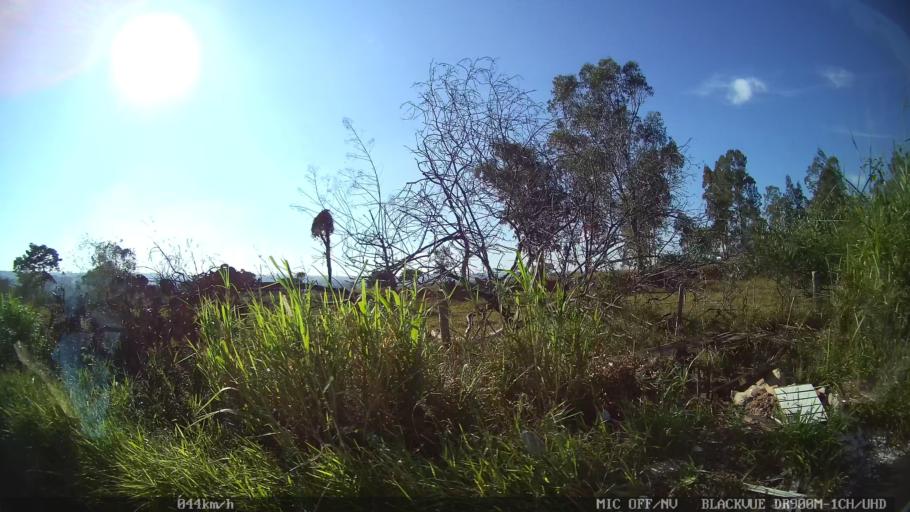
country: BR
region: Sao Paulo
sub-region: Campinas
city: Campinas
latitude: -22.9714
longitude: -47.1104
